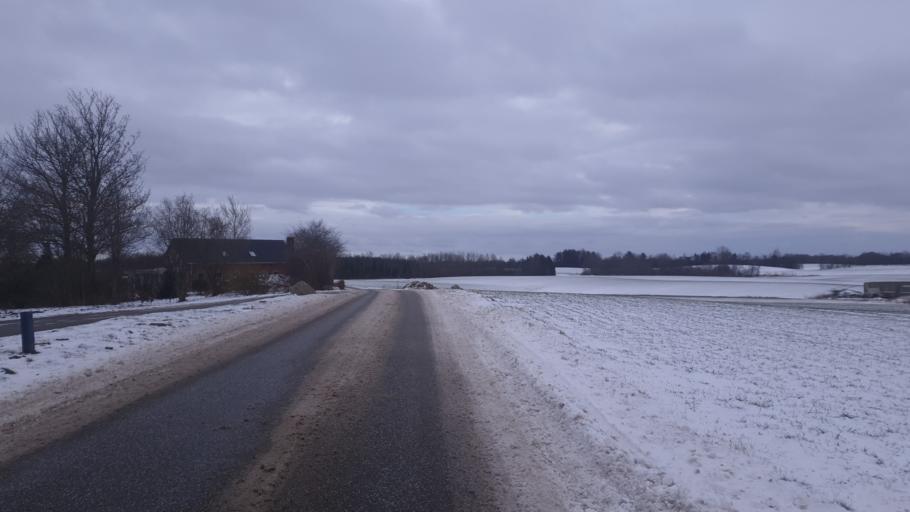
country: DK
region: Central Jutland
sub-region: Hedensted Kommune
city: Hedensted
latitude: 55.7937
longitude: 9.7049
